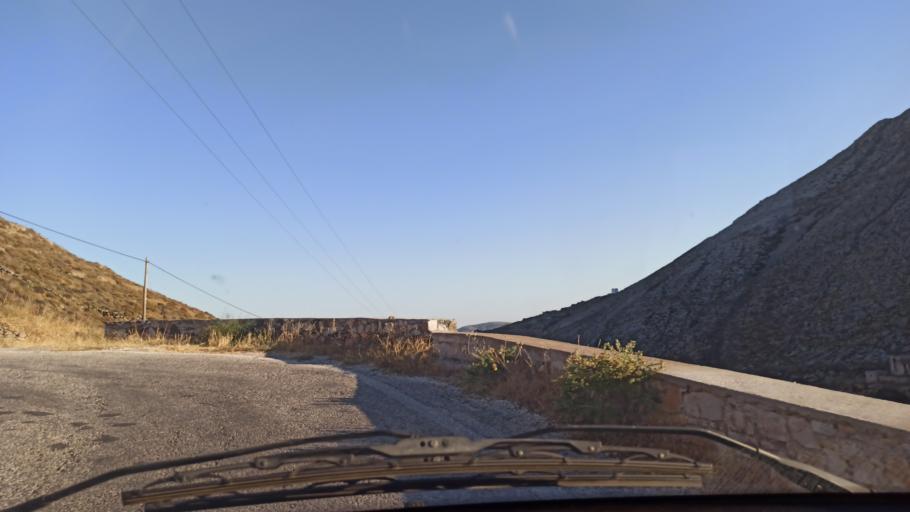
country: GR
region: South Aegean
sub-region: Nomos Kykladon
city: Ano Syros
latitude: 37.4597
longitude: 24.9317
